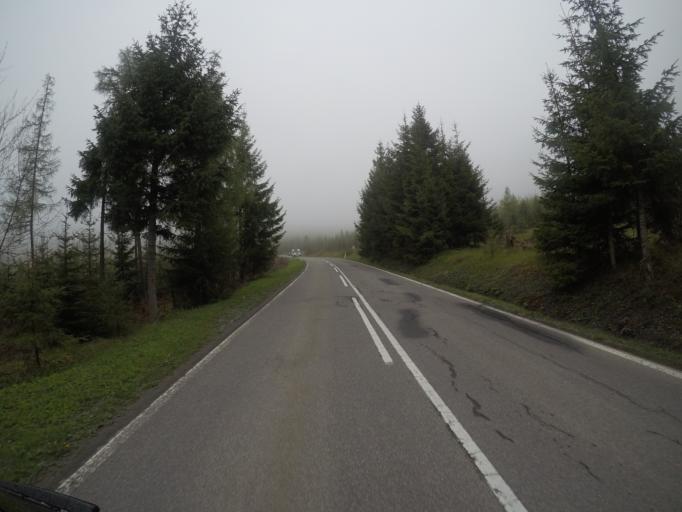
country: SK
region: Presovsky
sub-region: Okres Poprad
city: Strba
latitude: 49.1066
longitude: 20.0572
